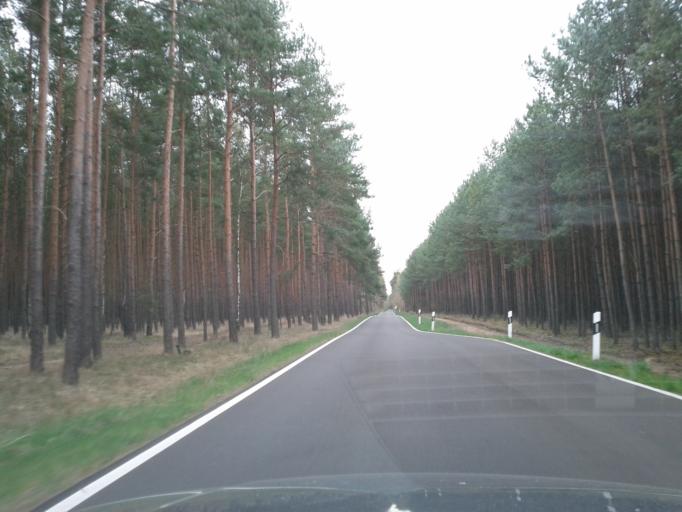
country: DE
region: Brandenburg
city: Spreenhagen
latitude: 52.3893
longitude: 13.8503
